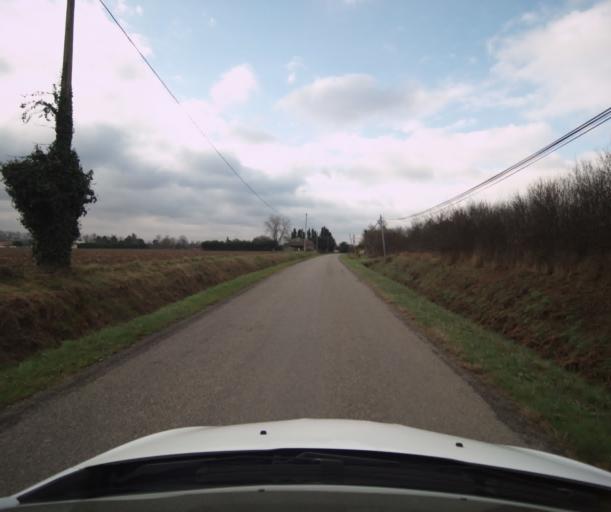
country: FR
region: Midi-Pyrenees
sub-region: Departement du Tarn-et-Garonne
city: Castelsarrasin
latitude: 44.0407
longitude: 1.1275
